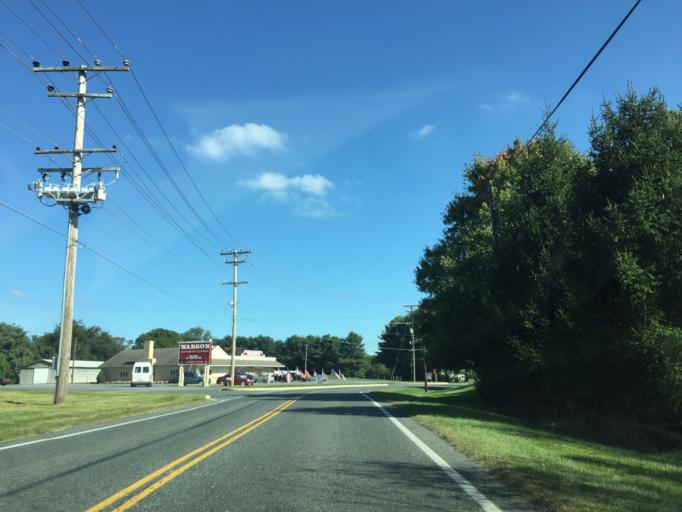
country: US
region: Maryland
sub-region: Harford County
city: Bel Air North
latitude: 39.5797
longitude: -76.3664
